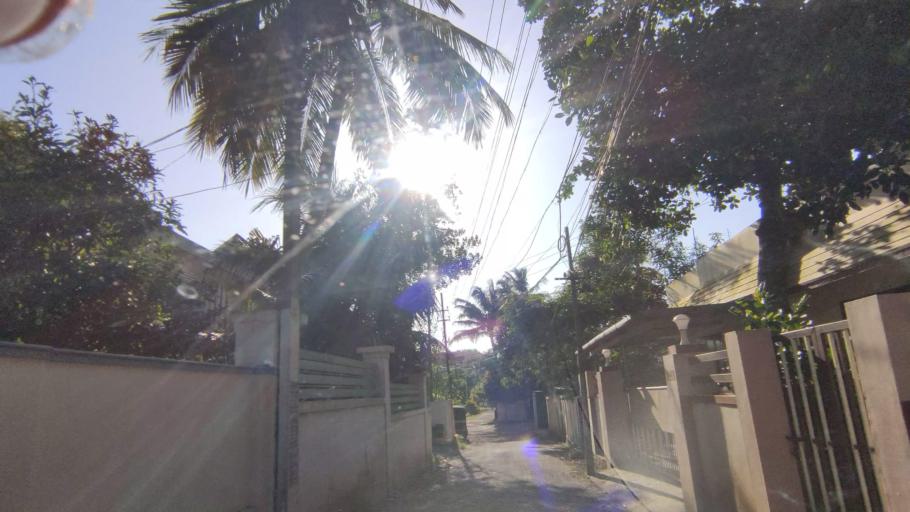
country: IN
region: Kerala
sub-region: Kottayam
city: Kottayam
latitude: 9.5929
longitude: 76.5093
